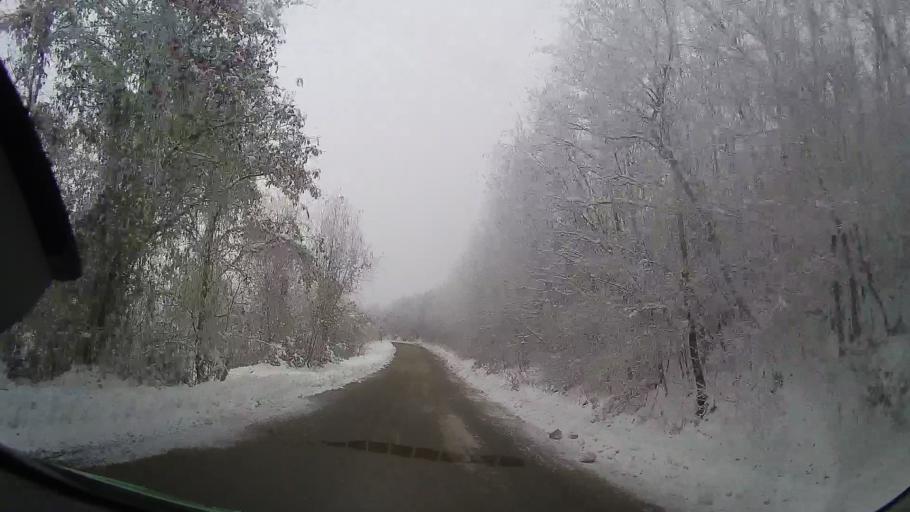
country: RO
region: Iasi
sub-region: Comuna Tansa
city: Suhulet
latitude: 46.8977
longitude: 27.2424
